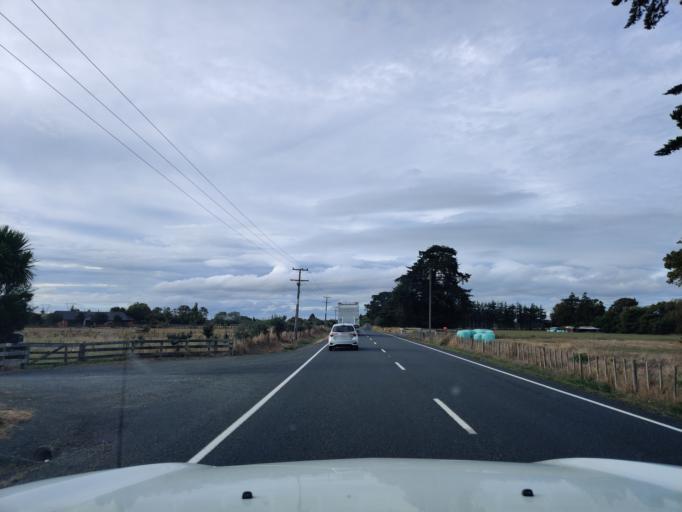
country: NZ
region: Waikato
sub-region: Hamilton City
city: Hamilton
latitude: -37.6976
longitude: 175.3381
